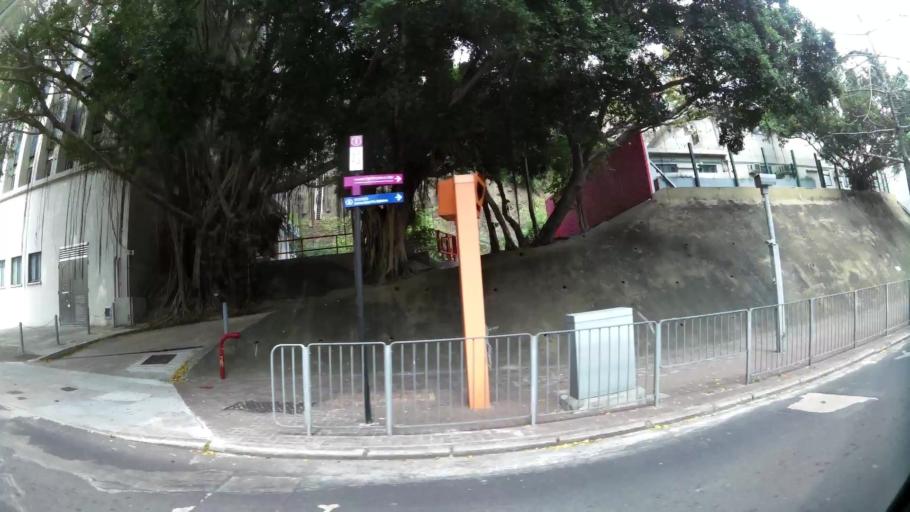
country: HK
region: Sham Shui Po
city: Sham Shui Po
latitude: 22.3351
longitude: 114.1627
